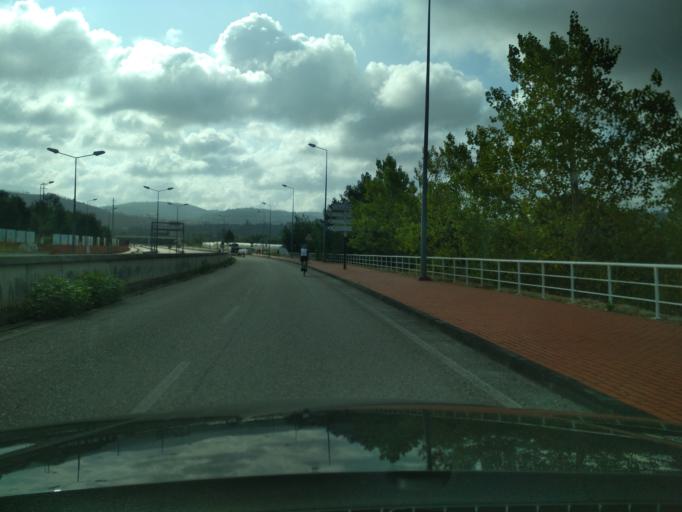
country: PT
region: Coimbra
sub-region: Coimbra
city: Coimbra
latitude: 40.1839
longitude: -8.4166
